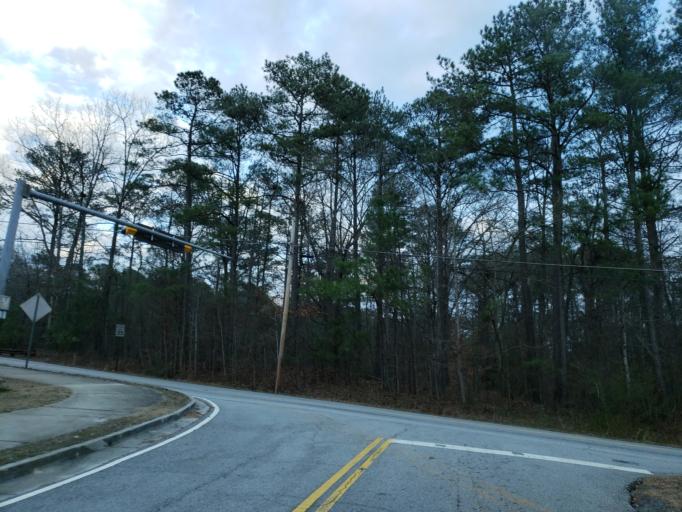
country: US
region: Georgia
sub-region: Cobb County
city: Mableton
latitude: 33.8524
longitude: -84.5582
